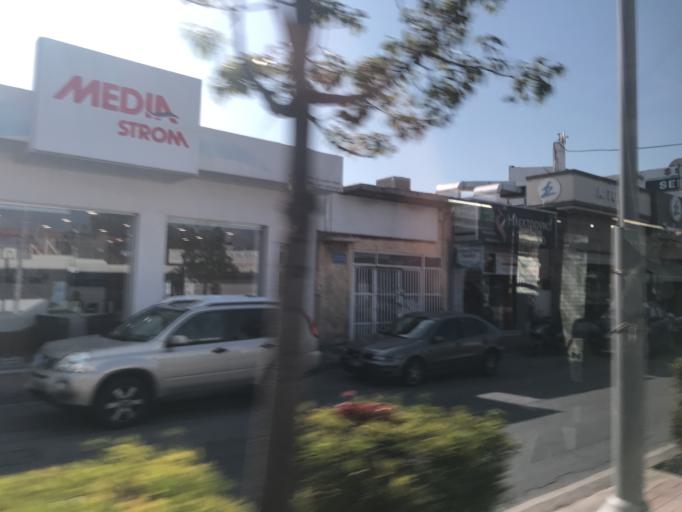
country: GR
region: Crete
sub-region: Nomos Irakleiou
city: Irakleion
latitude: 35.3319
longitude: 25.1128
